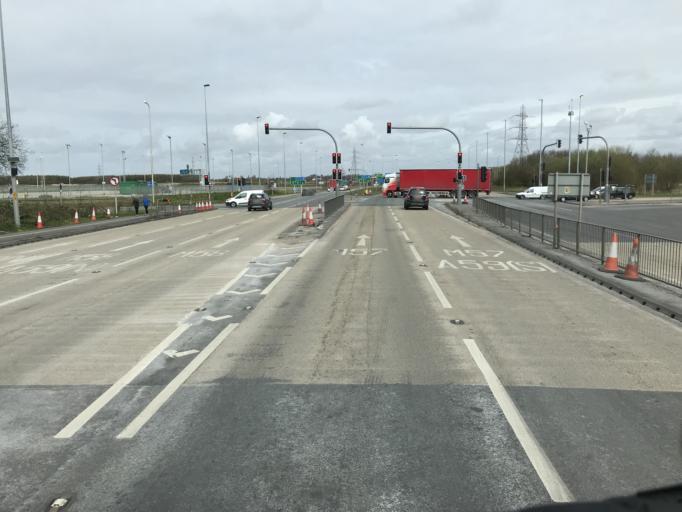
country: GB
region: England
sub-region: Sefton
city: Maghull
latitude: 53.4923
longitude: -2.9537
